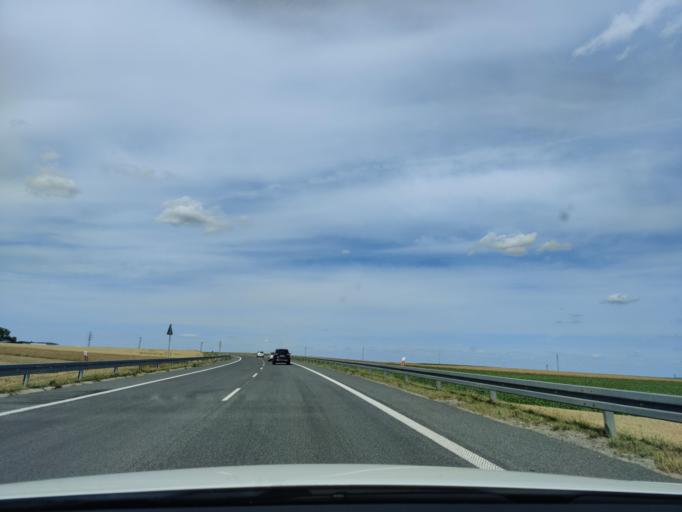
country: PL
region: Opole Voivodeship
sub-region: Powiat prudnicki
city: Biala
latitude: 50.3855
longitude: 17.6799
